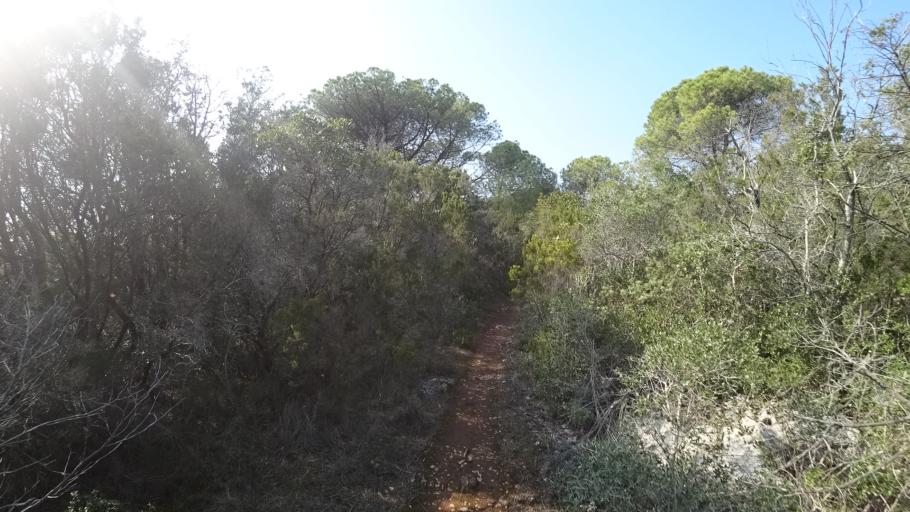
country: HR
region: Primorsko-Goranska
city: Mali Losinj
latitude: 44.4797
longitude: 14.5132
